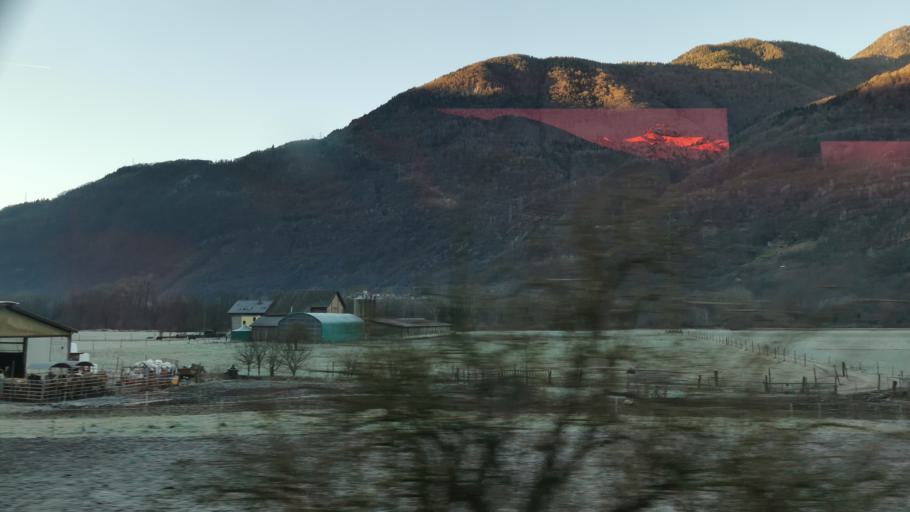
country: CH
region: Ticino
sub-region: Riviera District
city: Claro
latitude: 46.2436
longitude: 9.0284
